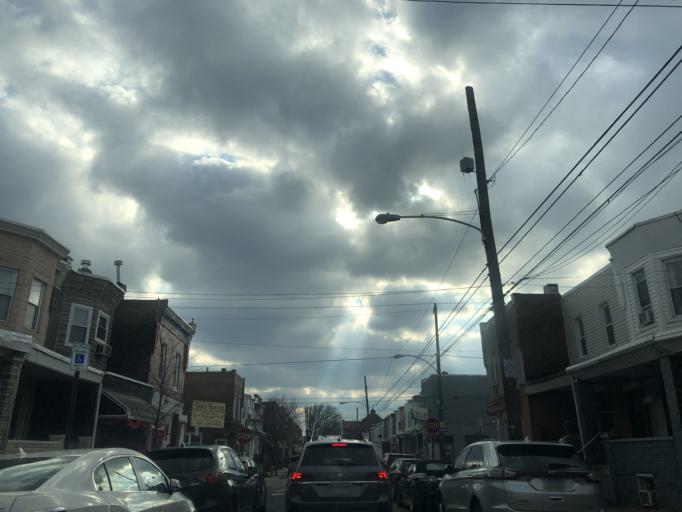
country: US
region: Pennsylvania
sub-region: Philadelphia County
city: Philadelphia
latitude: 39.9286
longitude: -75.1806
